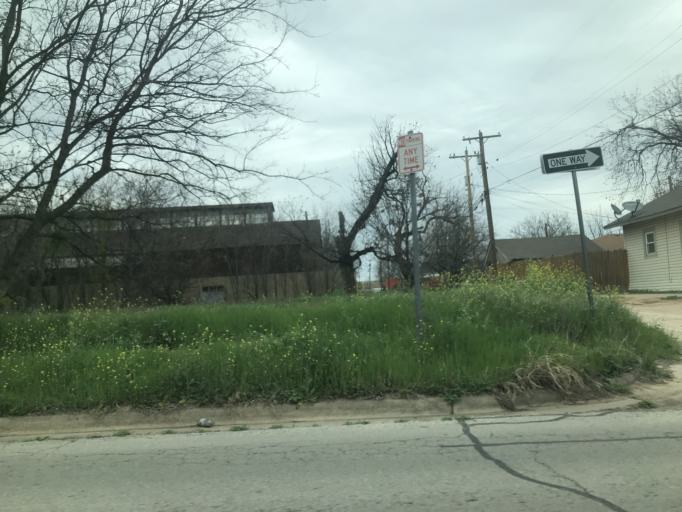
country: US
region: Texas
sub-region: Taylor County
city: Abilene
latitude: 32.4608
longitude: -99.7436
